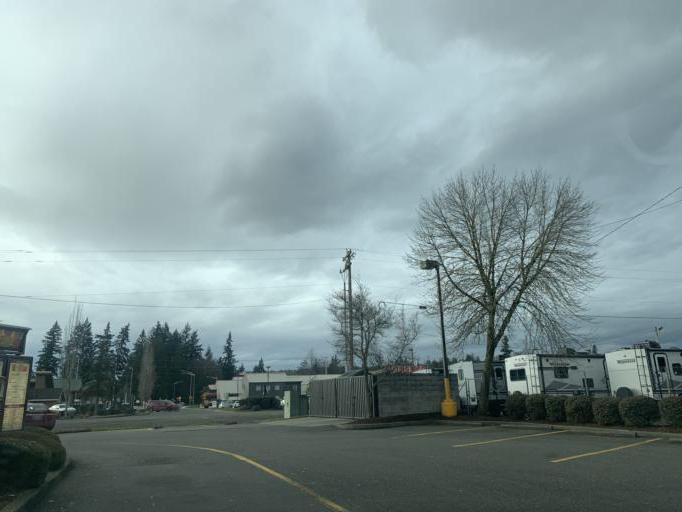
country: US
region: Washington
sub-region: Snohomish County
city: Marysville
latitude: 48.0541
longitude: -122.1865
